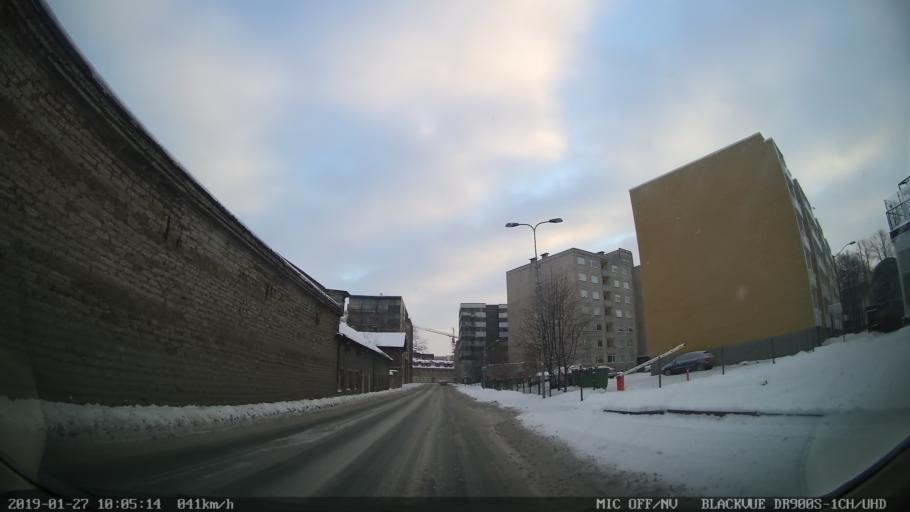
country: EE
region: Harju
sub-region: Tallinna linn
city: Tallinn
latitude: 59.4398
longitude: 24.7663
